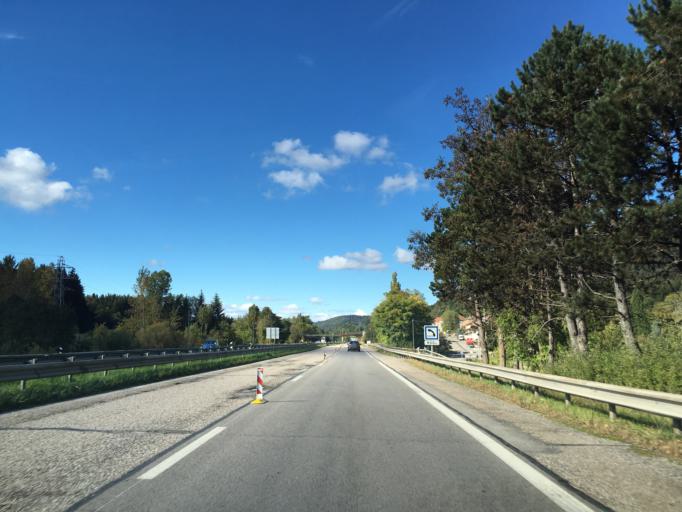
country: FR
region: Lorraine
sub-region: Departement des Vosges
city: Etival-Clairefontaine
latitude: 48.3815
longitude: 6.8709
